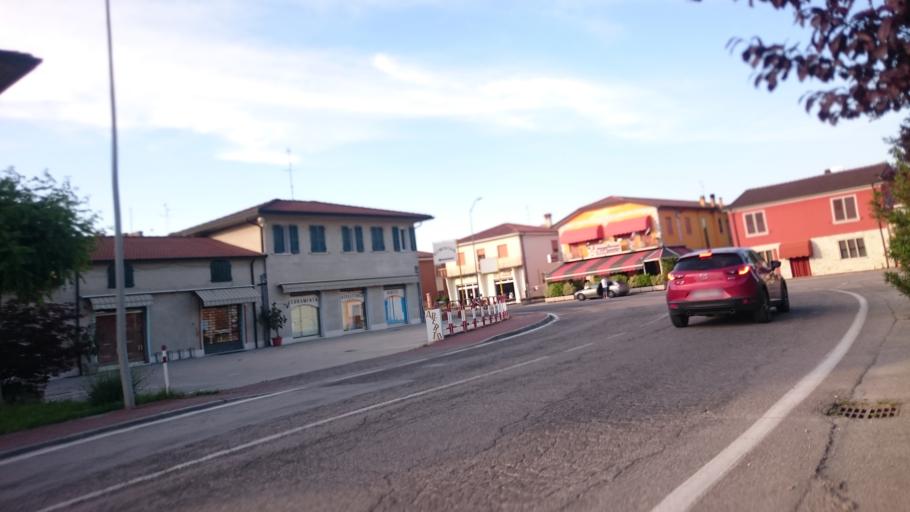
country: IT
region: Veneto
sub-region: Provincia di Verona
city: Roncanova
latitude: 45.1480
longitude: 11.1151
